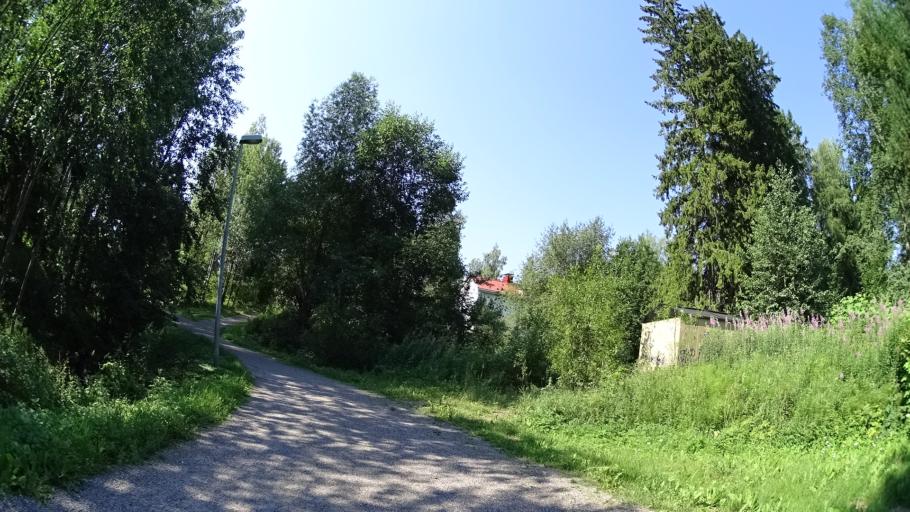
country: FI
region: Uusimaa
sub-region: Helsinki
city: Kerava
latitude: 60.3763
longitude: 25.0858
